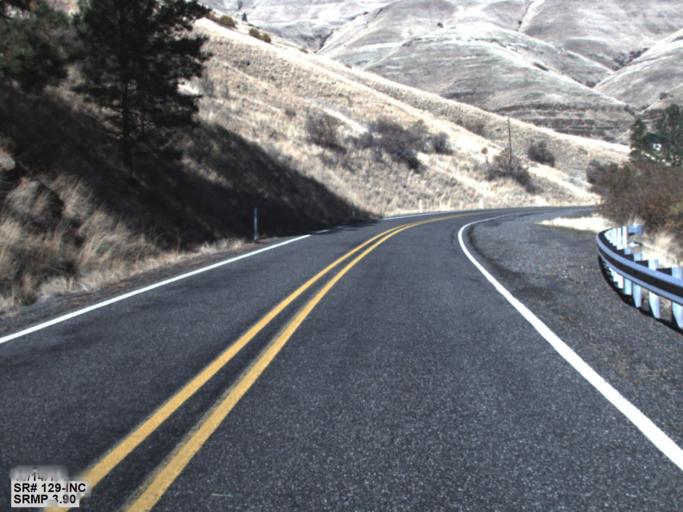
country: US
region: Washington
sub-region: Asotin County
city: Asotin
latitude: 46.0355
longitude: -117.2552
